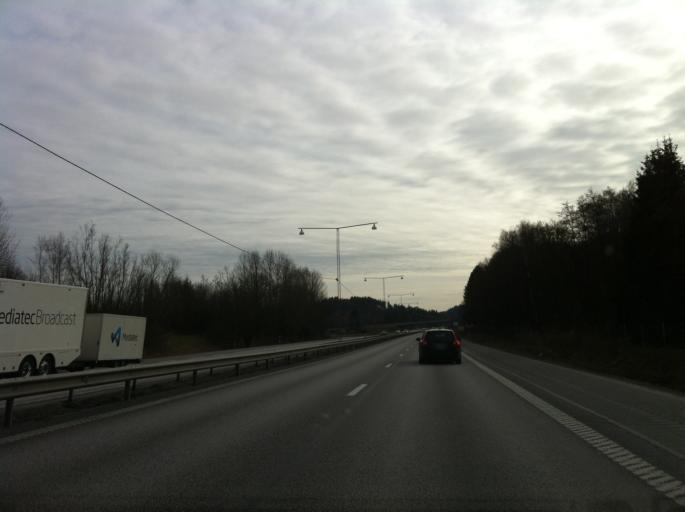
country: SE
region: Vaestra Goetaland
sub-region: Molndal
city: Kallered
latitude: 57.6316
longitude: 12.0347
